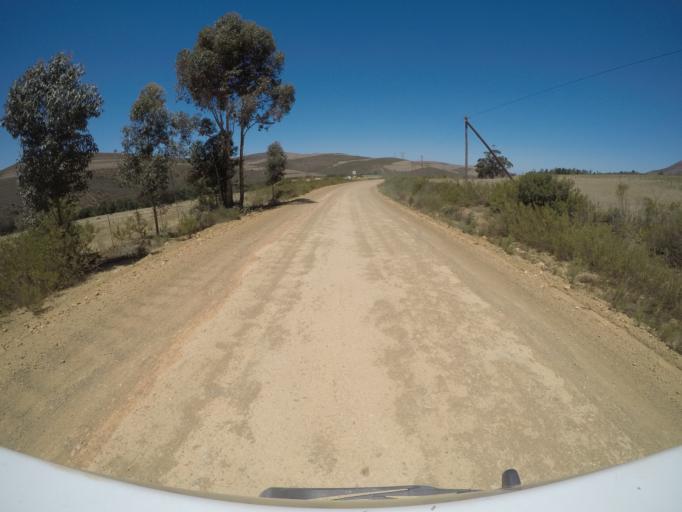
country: ZA
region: Western Cape
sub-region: Overberg District Municipality
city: Caledon
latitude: -34.1918
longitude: 19.2252
